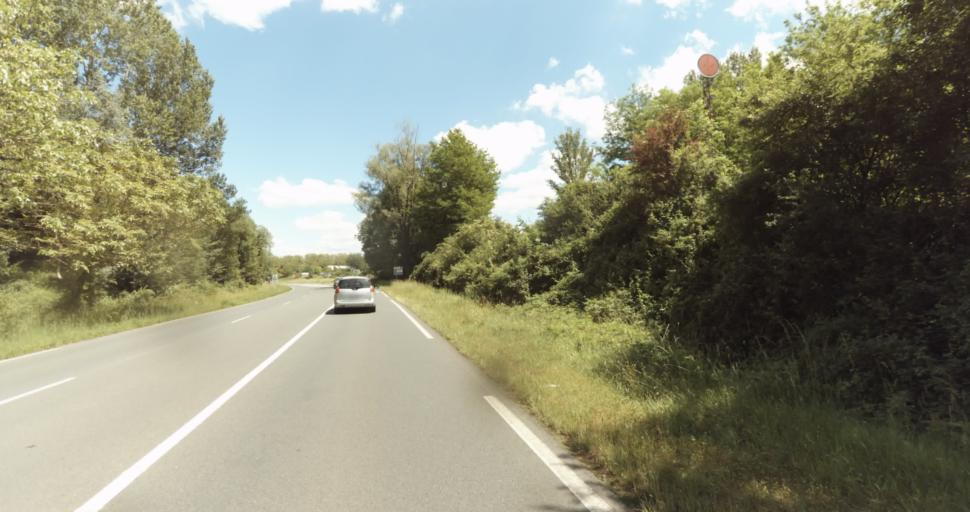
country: FR
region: Aquitaine
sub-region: Departement de la Dordogne
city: Belves
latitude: 44.8216
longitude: 0.9648
